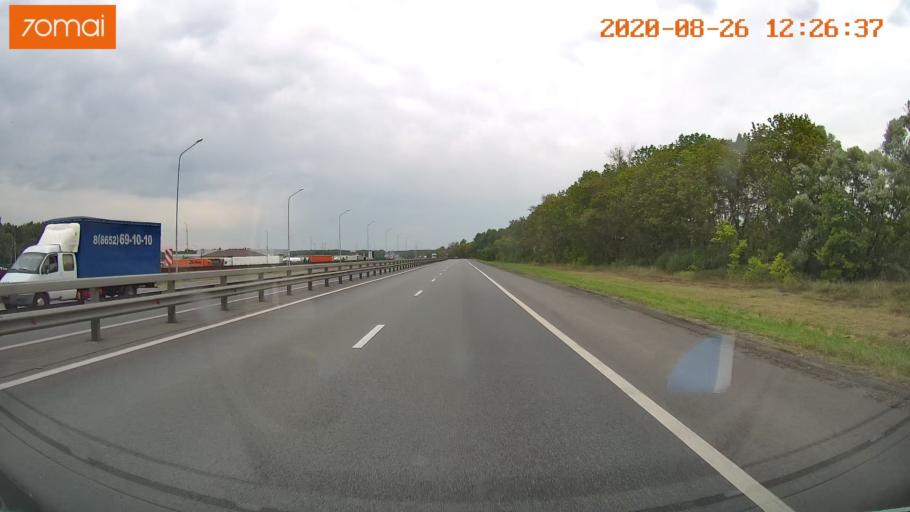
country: RU
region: Rjazan
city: Polyany
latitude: 54.5365
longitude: 39.8565
